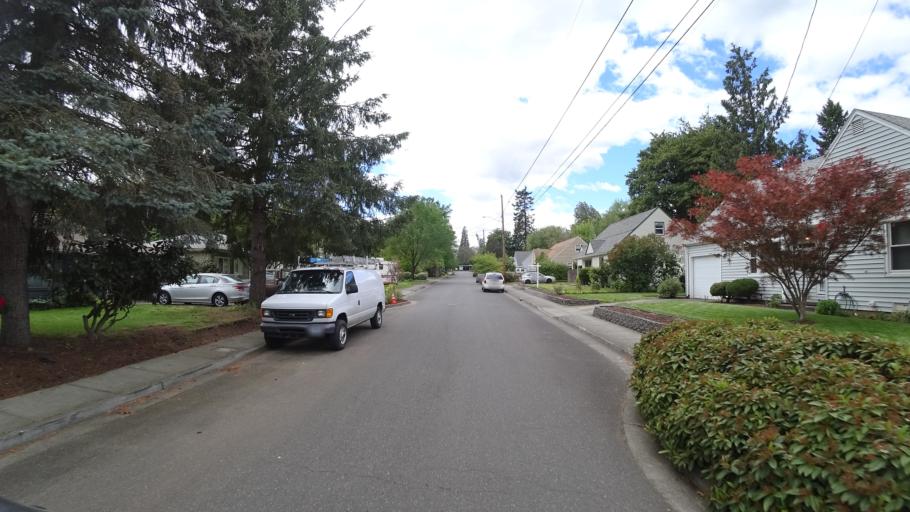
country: US
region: Oregon
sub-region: Washington County
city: Beaverton
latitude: 45.4779
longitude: -122.7981
